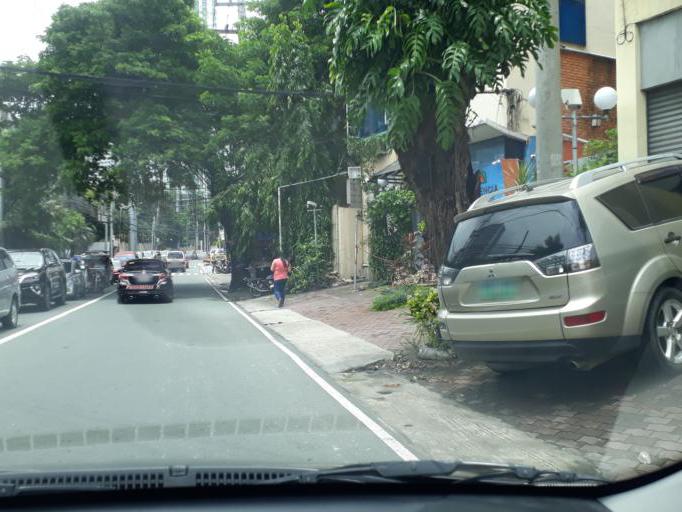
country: PH
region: Metro Manila
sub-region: San Juan
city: San Juan
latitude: 14.6110
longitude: 121.0335
